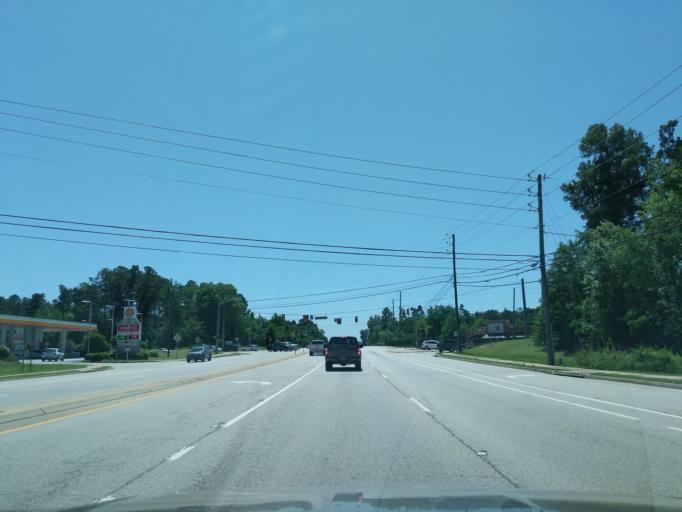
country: US
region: Georgia
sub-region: Columbia County
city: Martinez
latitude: 33.5509
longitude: -82.0906
